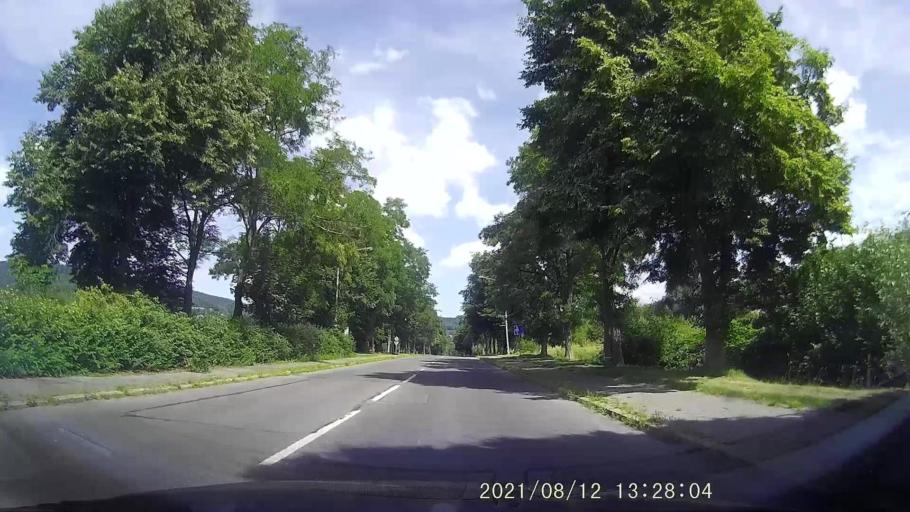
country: PL
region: Lower Silesian Voivodeship
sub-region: Powiat klodzki
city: Ladek-Zdroj
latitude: 50.3405
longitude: 16.8726
